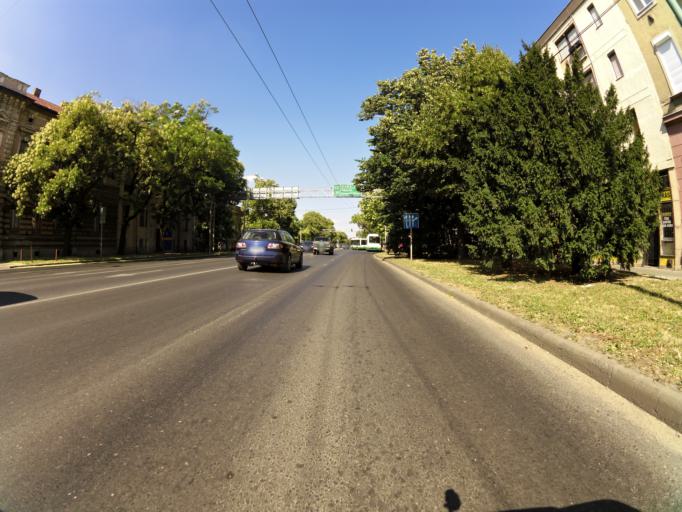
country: HU
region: Csongrad
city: Szeged
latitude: 46.2587
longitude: 20.1434
